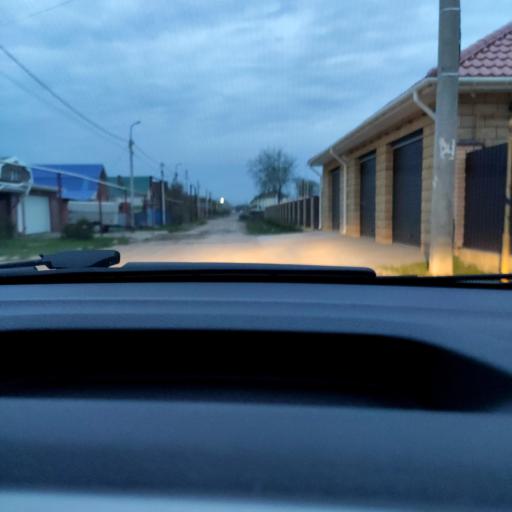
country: RU
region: Samara
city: Tol'yatti
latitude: 53.5501
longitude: 49.3976
